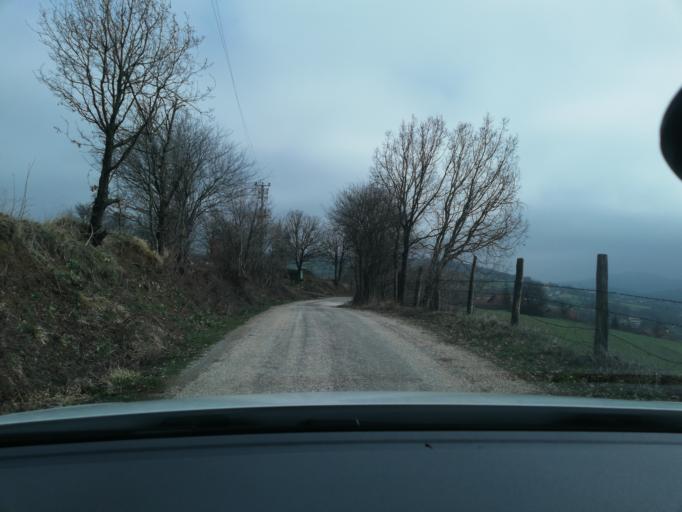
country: TR
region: Bolu
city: Bolu
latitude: 40.6669
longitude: 31.4661
